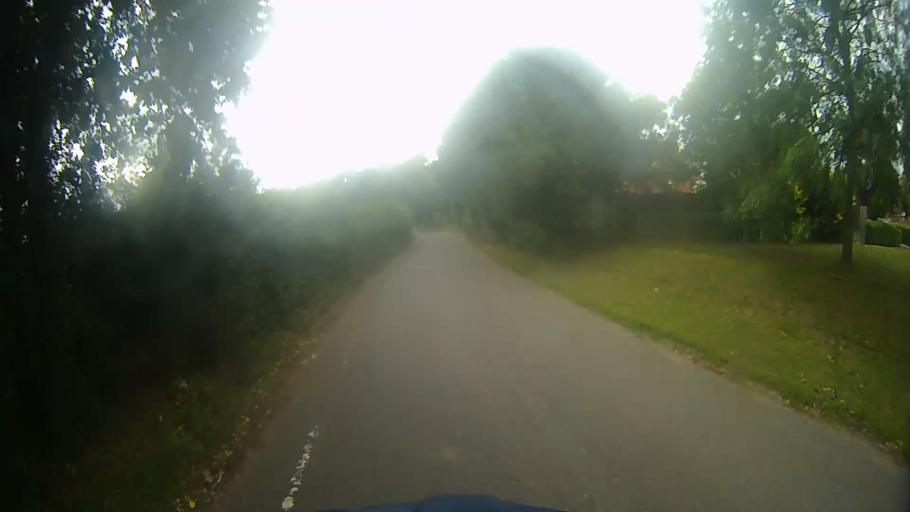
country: GB
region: England
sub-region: Hampshire
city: Kingsley
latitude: 51.1911
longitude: -0.8806
